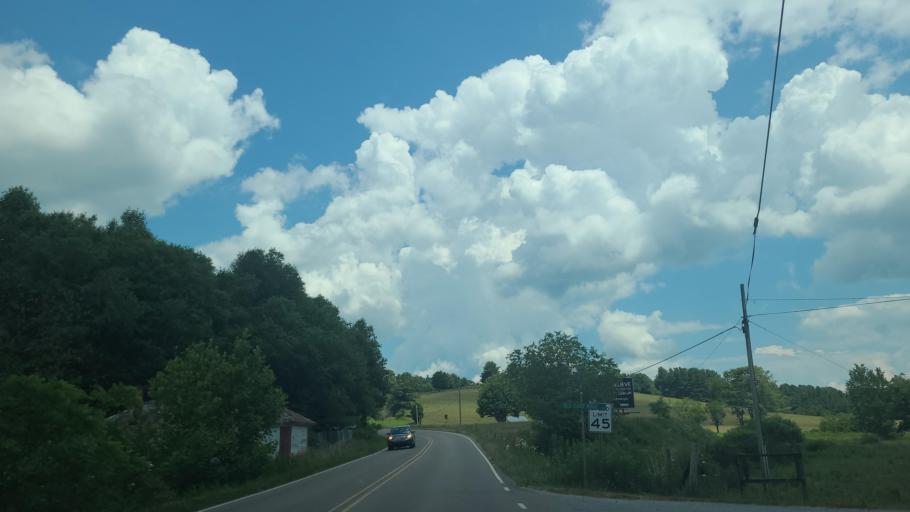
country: US
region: North Carolina
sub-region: Watauga County
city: Boone
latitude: 36.2333
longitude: -81.5498
